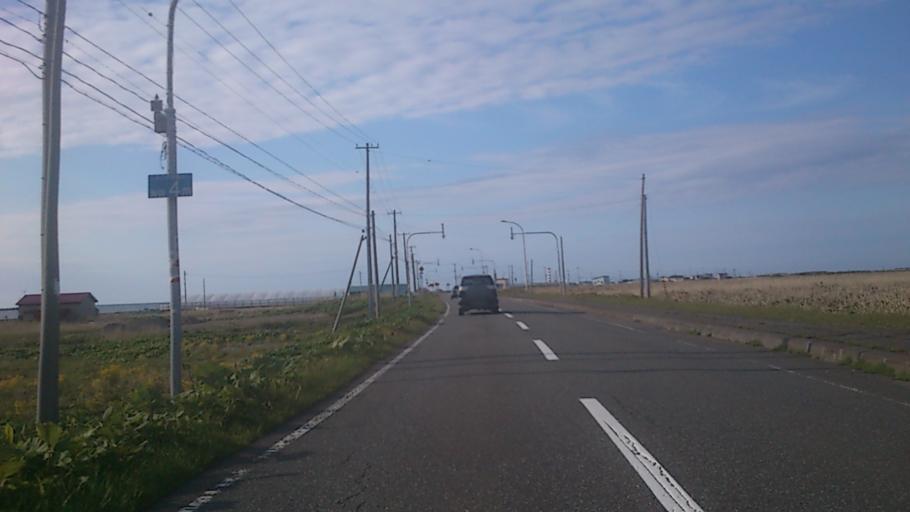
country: JP
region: Hokkaido
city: Wakkanai
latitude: 45.4329
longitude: 141.6398
